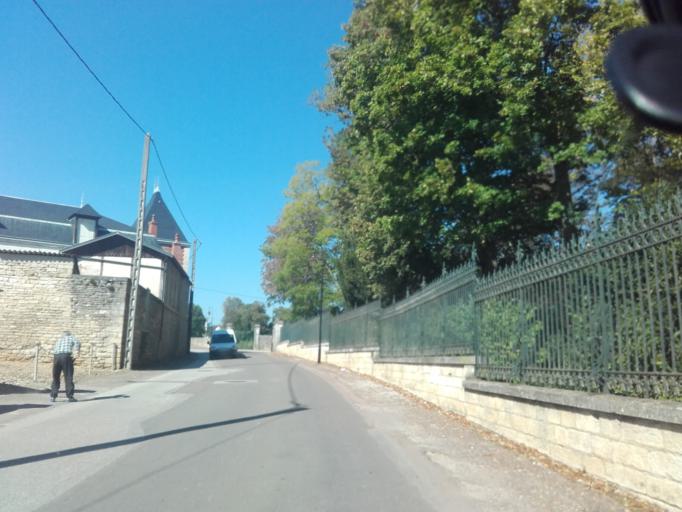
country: FR
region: Bourgogne
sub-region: Departement de la Cote-d'Or
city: Meursault
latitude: 46.9775
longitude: 4.7744
